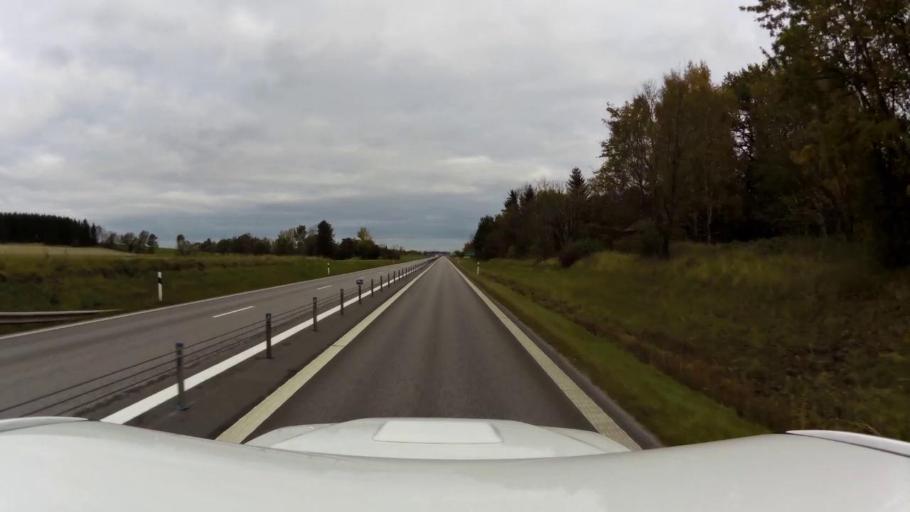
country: SE
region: OEstergoetland
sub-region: Linkopings Kommun
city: Berg
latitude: 58.4690
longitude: 15.4930
